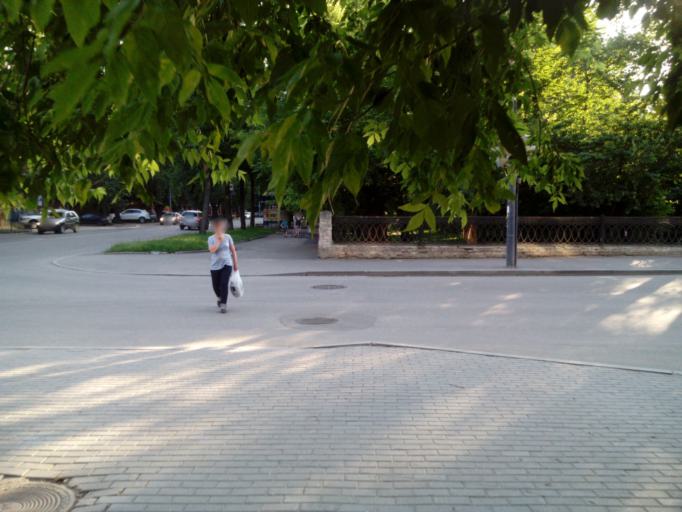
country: RU
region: Sverdlovsk
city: Yekaterinburg
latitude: 56.8469
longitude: 60.6549
